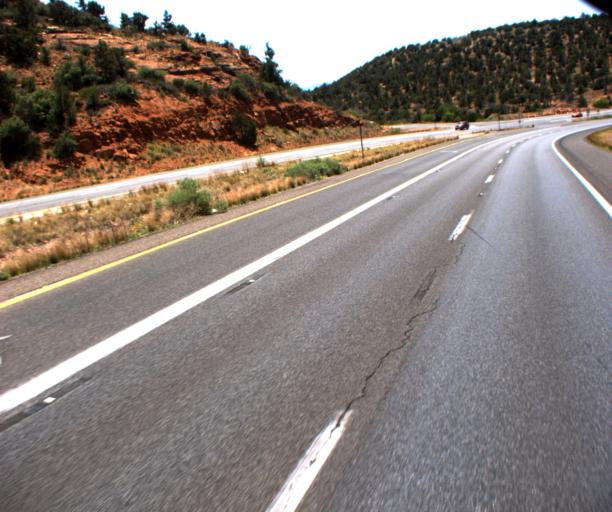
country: US
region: Arizona
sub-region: Yavapai County
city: West Sedona
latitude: 34.8454
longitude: -111.8478
